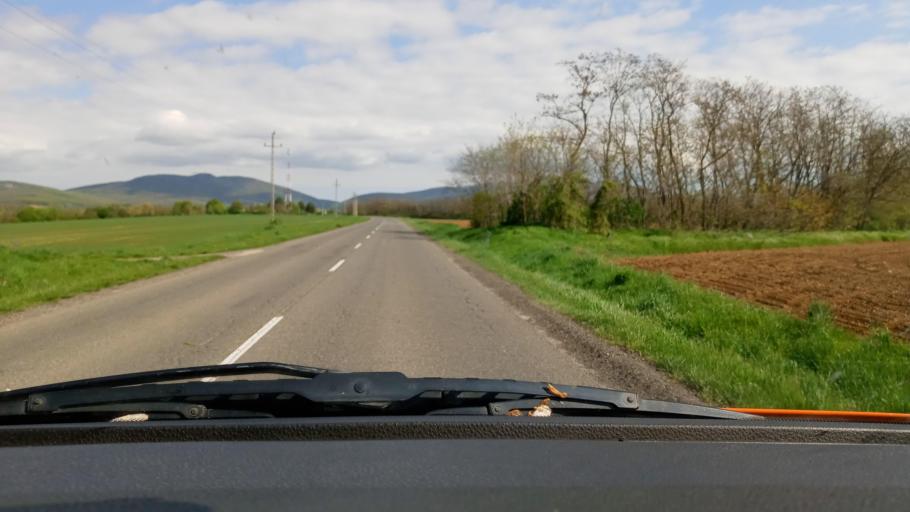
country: HU
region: Baranya
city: Hosszuheteny
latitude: 46.1201
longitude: 18.3483
